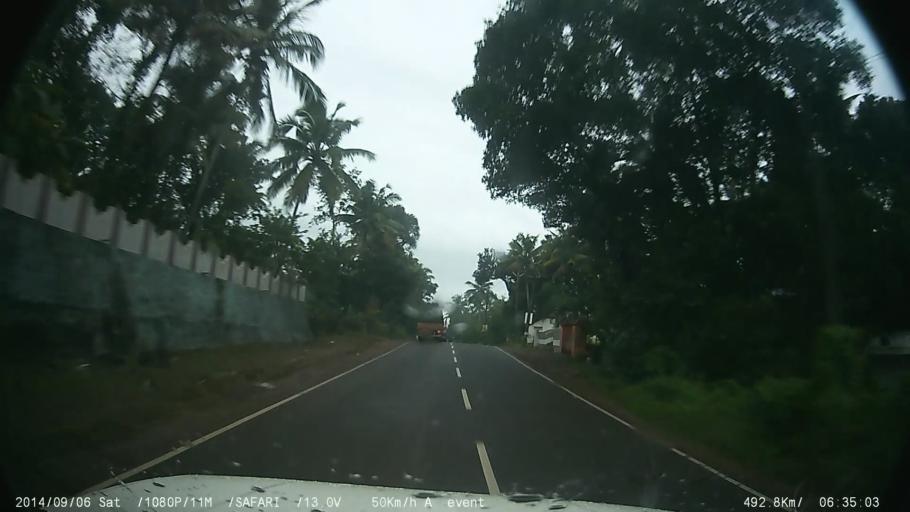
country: IN
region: Kerala
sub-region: Kottayam
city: Vaikam
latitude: 9.7874
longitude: 76.4585
